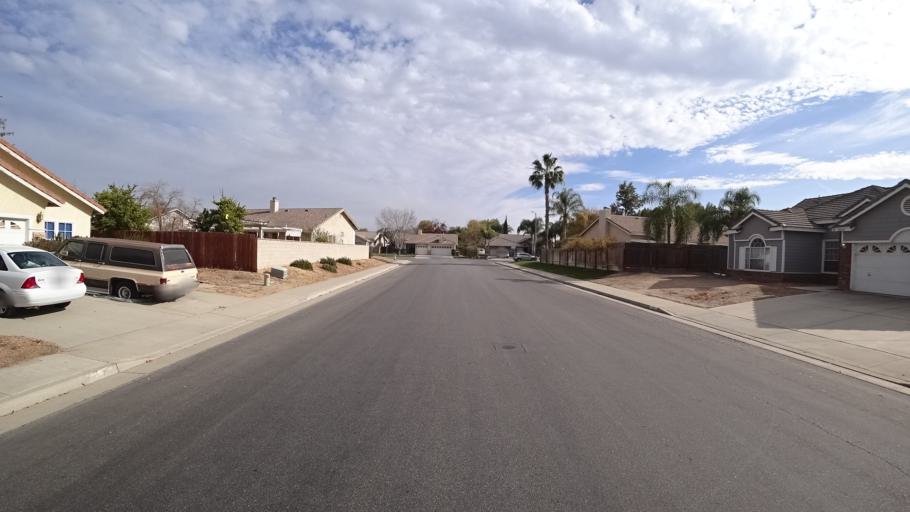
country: US
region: California
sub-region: Kern County
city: Greenacres
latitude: 35.4093
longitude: -119.1162
